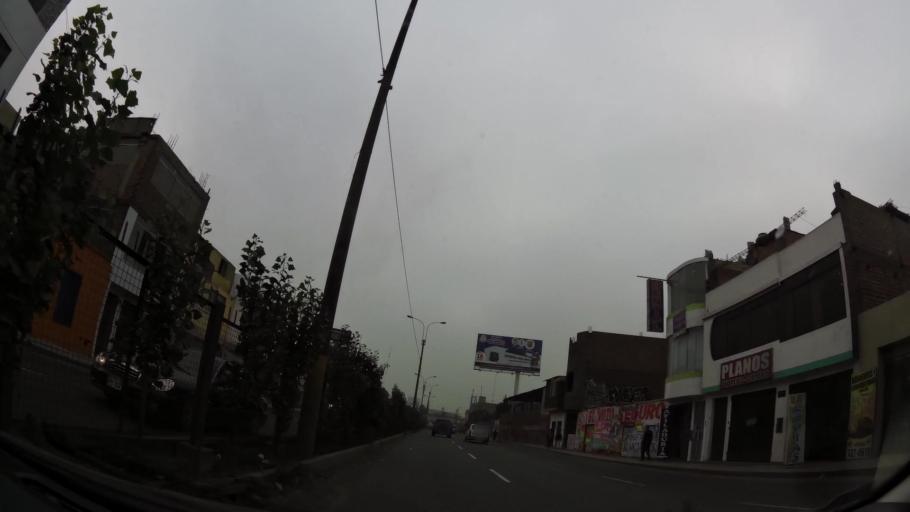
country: PE
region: Lima
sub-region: Lima
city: Vitarte
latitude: -12.0249
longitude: -76.9170
